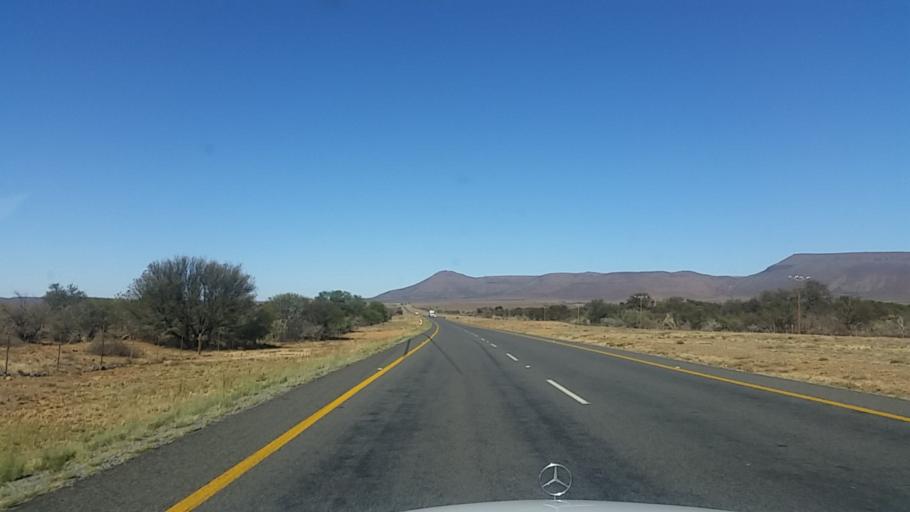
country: ZA
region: Eastern Cape
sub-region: Cacadu District Municipality
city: Graaff-Reinet
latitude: -32.0026
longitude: 24.6641
